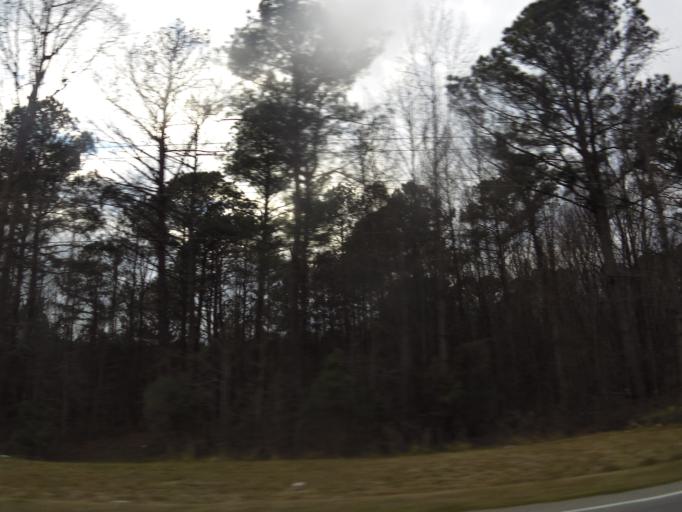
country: US
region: North Carolina
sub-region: Nash County
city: Rocky Mount
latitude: 36.0251
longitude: -77.7686
